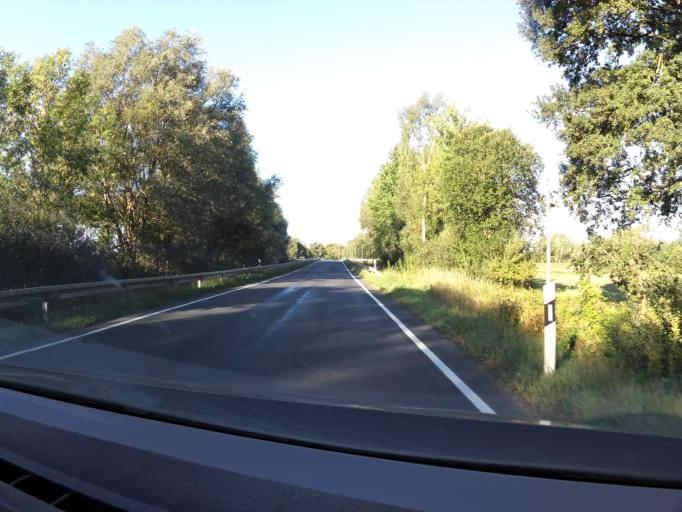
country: DE
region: Mecklenburg-Vorpommern
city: Alt-Sanitz
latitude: 53.8250
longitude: 13.5240
